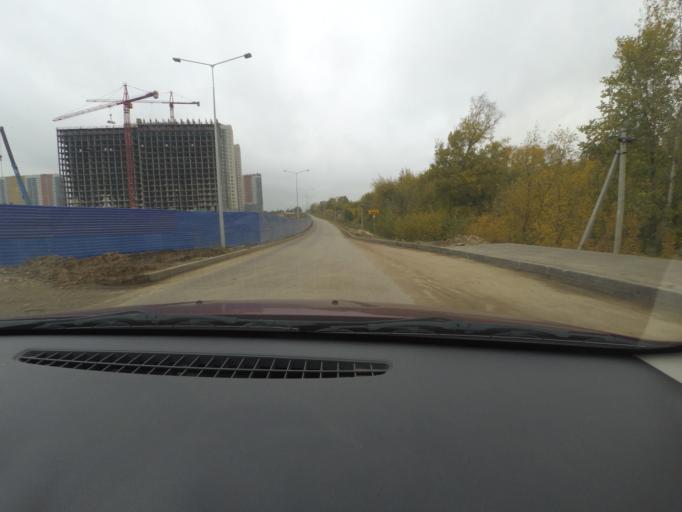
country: RU
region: Nizjnij Novgorod
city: Afonino
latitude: 56.2485
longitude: 44.0516
